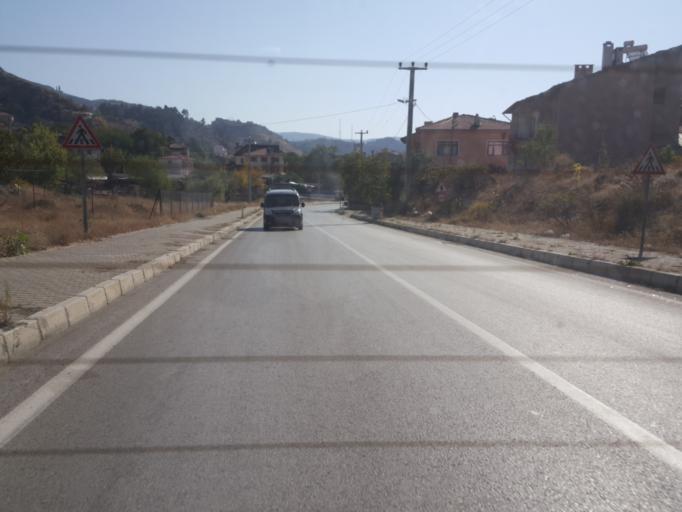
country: TR
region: Corum
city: Iskilip
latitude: 40.7373
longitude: 34.4605
